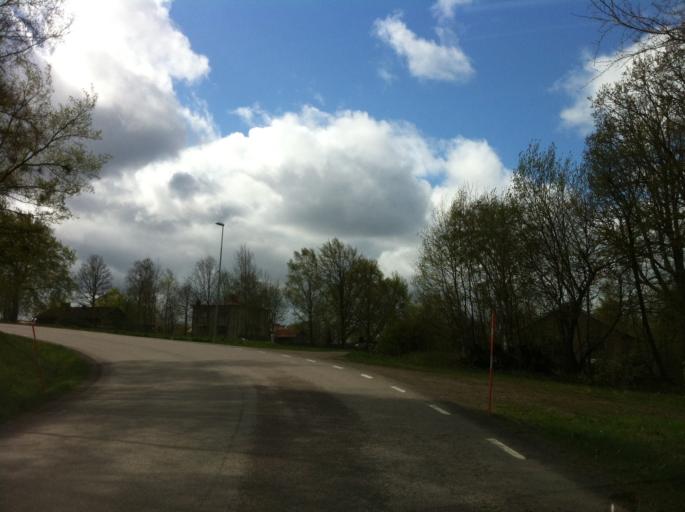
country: SE
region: Vaestra Goetaland
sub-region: Alingsas Kommun
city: Ingared
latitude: 57.8184
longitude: 12.5588
